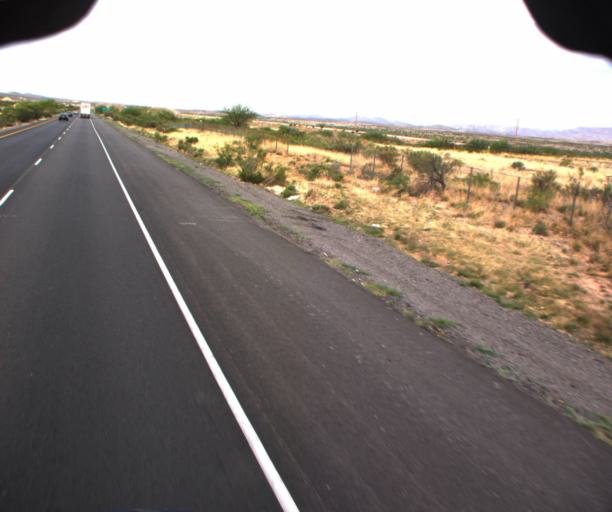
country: US
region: Arizona
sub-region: Cochise County
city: Mescal
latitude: 31.9797
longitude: -110.5222
